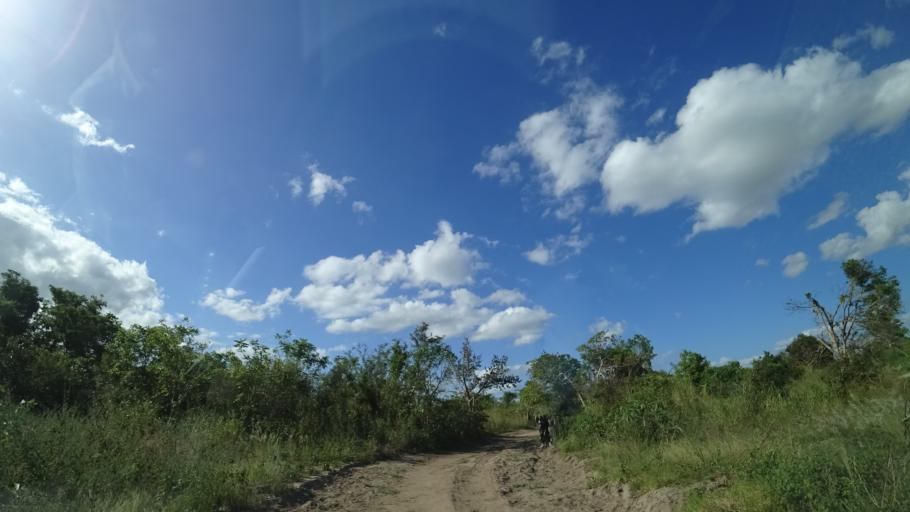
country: MZ
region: Sofala
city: Dondo
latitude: -19.4221
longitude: 34.7150
